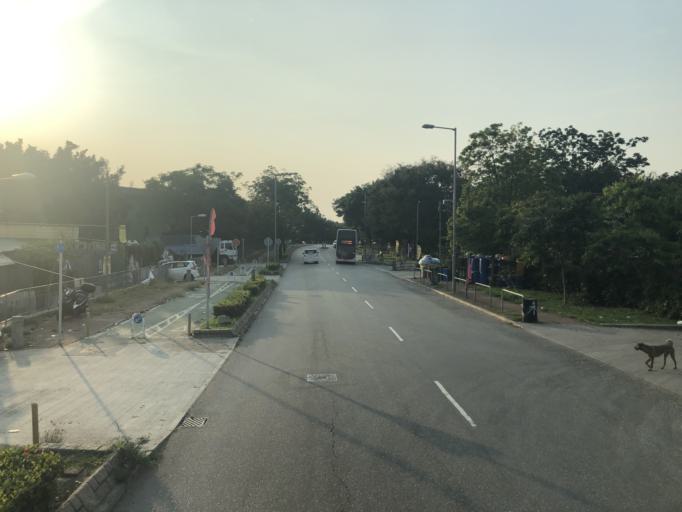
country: HK
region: Yuen Long
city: Yuen Long Kau Hui
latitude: 22.4552
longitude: 113.9932
